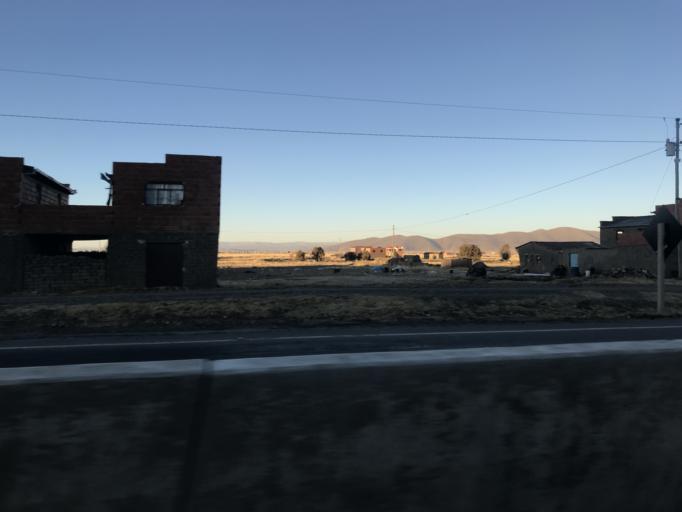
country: BO
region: La Paz
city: Batallas
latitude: -16.2994
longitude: -68.5092
